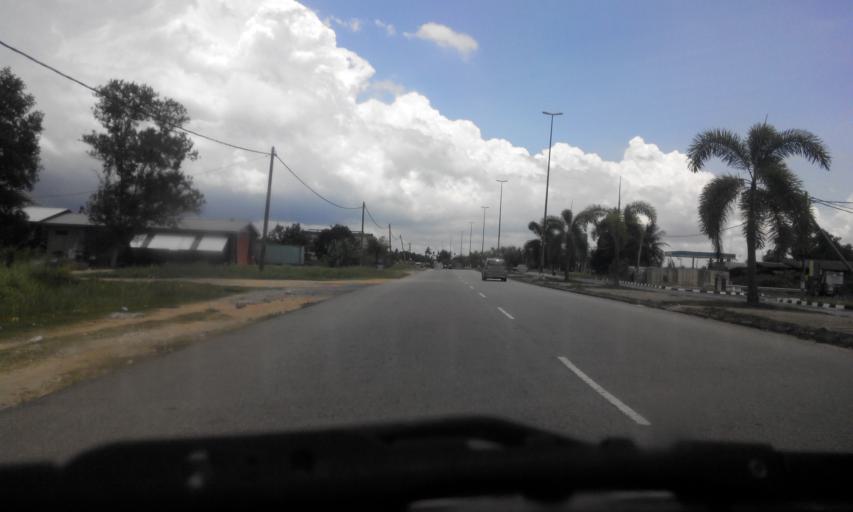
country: MY
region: Perak
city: Parit Buntar
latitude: 5.1299
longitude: 100.5003
